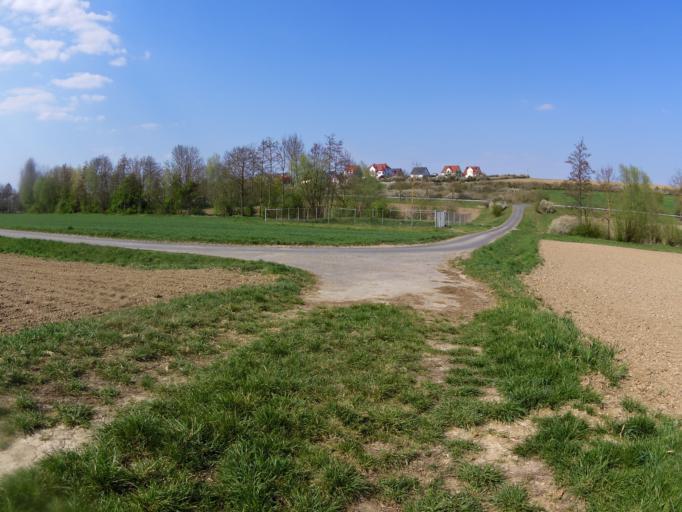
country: DE
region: Bavaria
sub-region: Regierungsbezirk Unterfranken
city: Dettelbach
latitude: 49.8209
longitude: 10.1315
